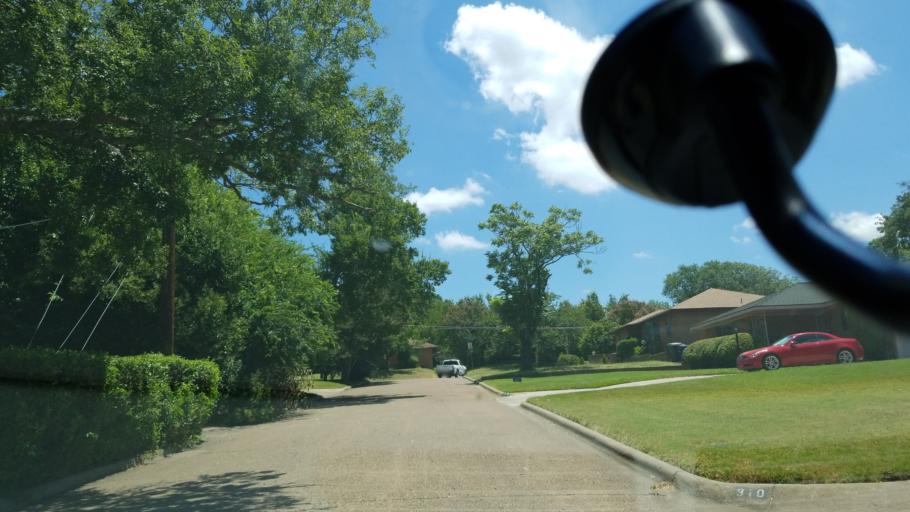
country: US
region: Texas
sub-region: Dallas County
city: Cockrell Hill
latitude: 32.6764
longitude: -96.8201
